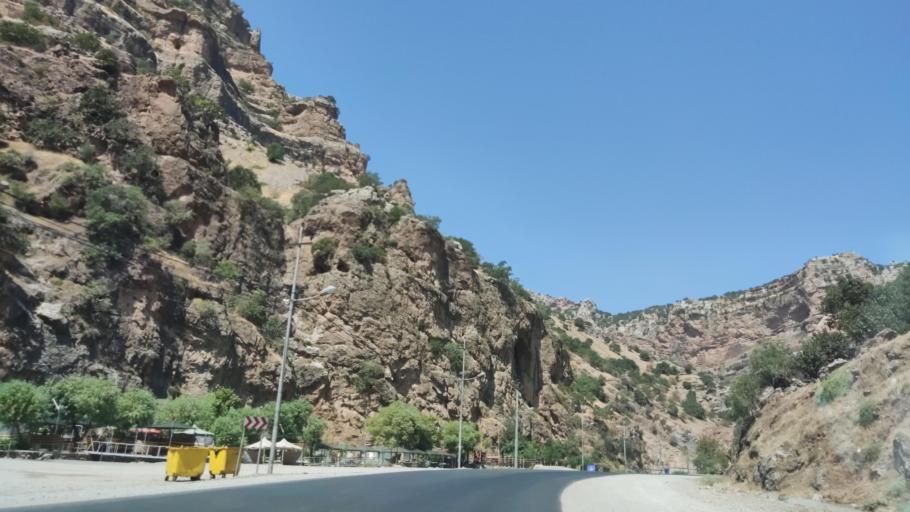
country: IQ
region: Arbil
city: Ruwandiz
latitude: 36.6277
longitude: 44.4507
